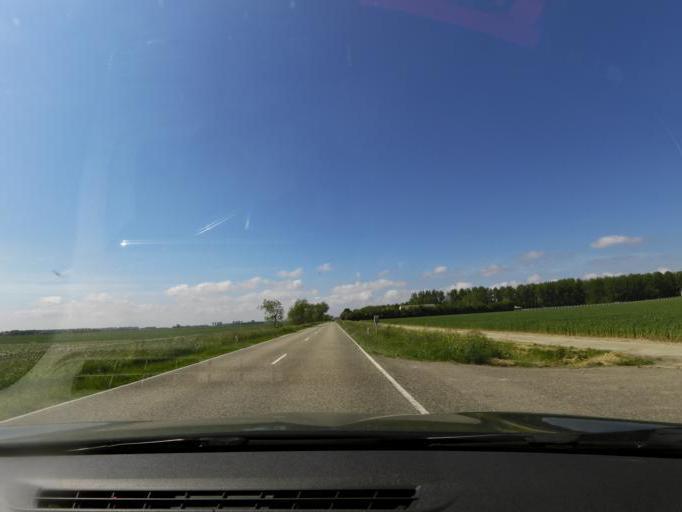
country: NL
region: South Holland
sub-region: Gemeente Goeree-Overflakkee
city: Dirksland
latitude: 51.7862
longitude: 4.0617
